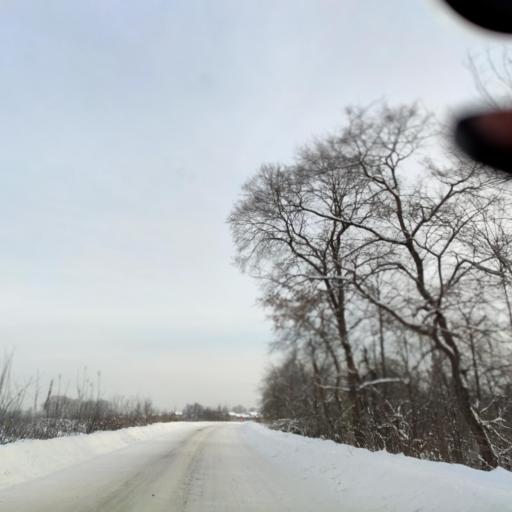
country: RU
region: Bashkortostan
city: Mikhaylovka
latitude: 54.7486
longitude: 55.8749
